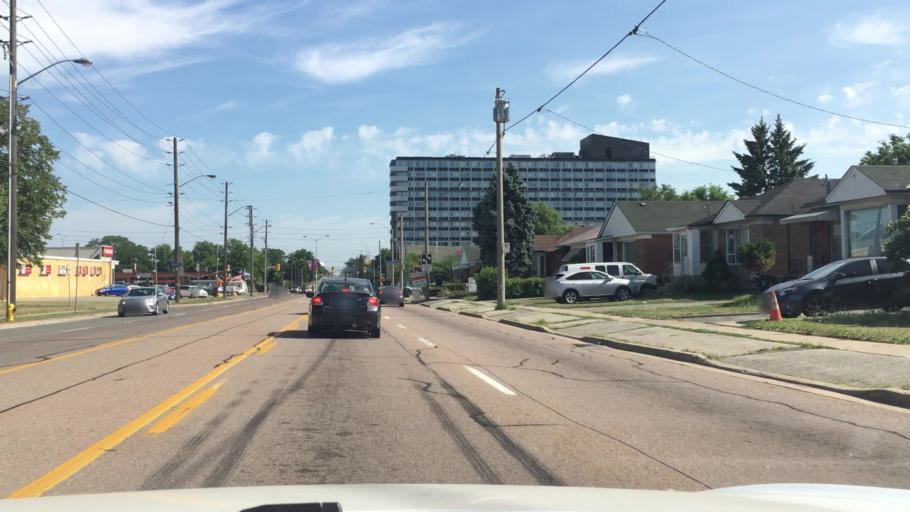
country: CA
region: Ontario
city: Scarborough
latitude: 43.7471
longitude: -79.2956
